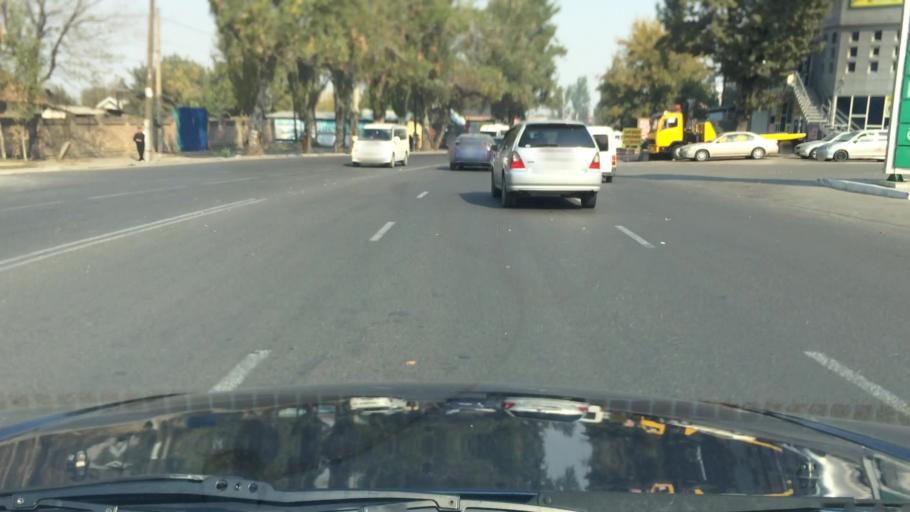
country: KG
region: Chuy
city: Lebedinovka
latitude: 42.8757
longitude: 74.6370
